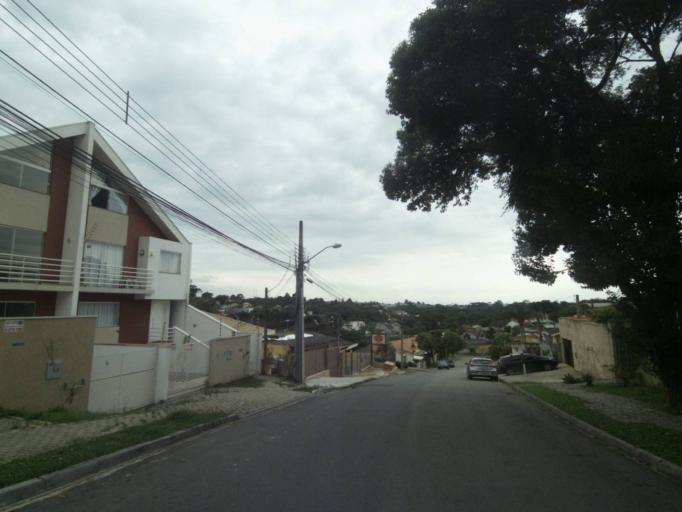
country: BR
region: Parana
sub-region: Curitiba
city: Curitiba
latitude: -25.3952
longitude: -49.2917
